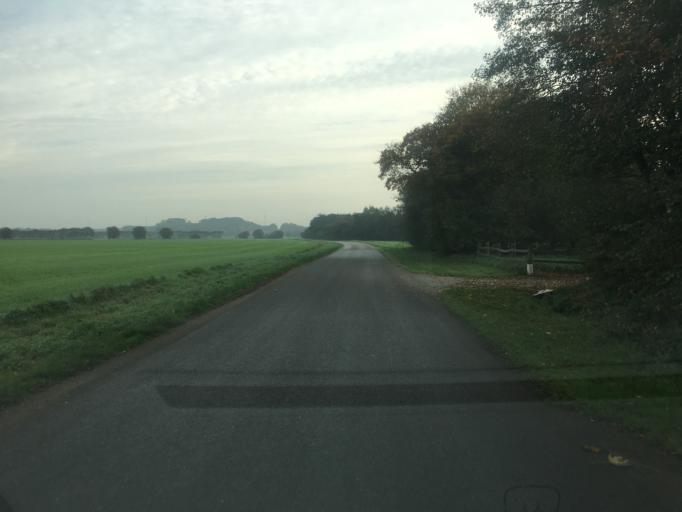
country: DK
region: South Denmark
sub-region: Tonder Kommune
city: Toftlund
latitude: 55.1027
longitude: 9.0682
